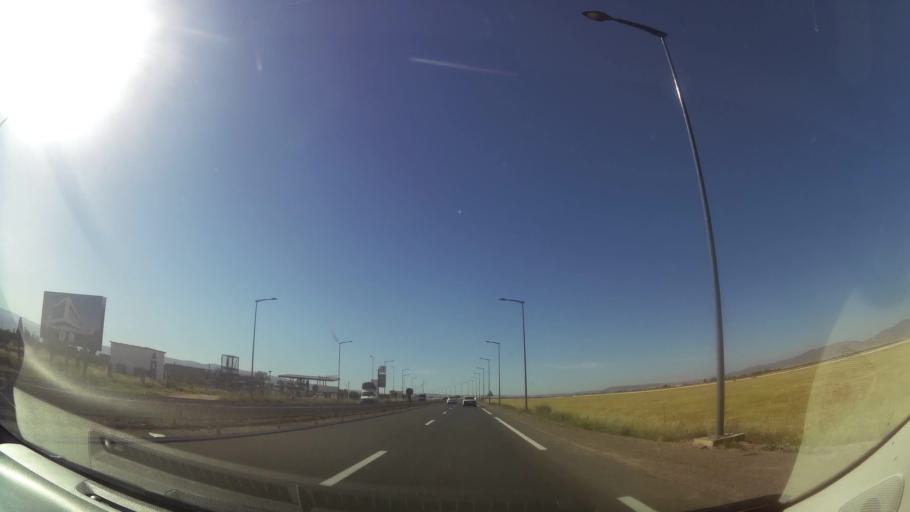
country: MA
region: Oriental
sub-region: Oujda-Angad
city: Oujda
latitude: 34.8052
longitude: -1.9578
